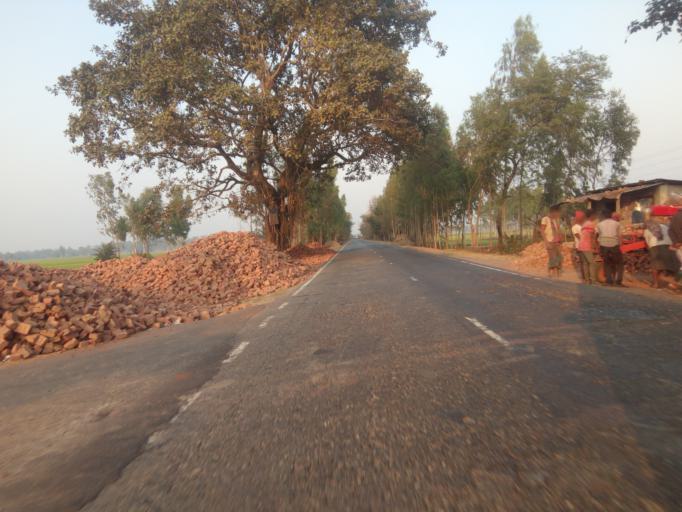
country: BD
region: Rajshahi
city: Bogra
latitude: 24.5777
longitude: 89.2217
